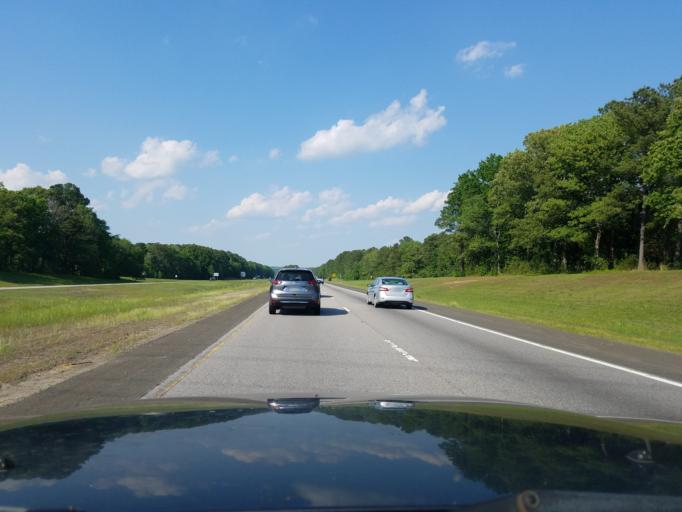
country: US
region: North Carolina
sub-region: Granville County
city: Butner
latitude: 36.1477
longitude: -78.7246
